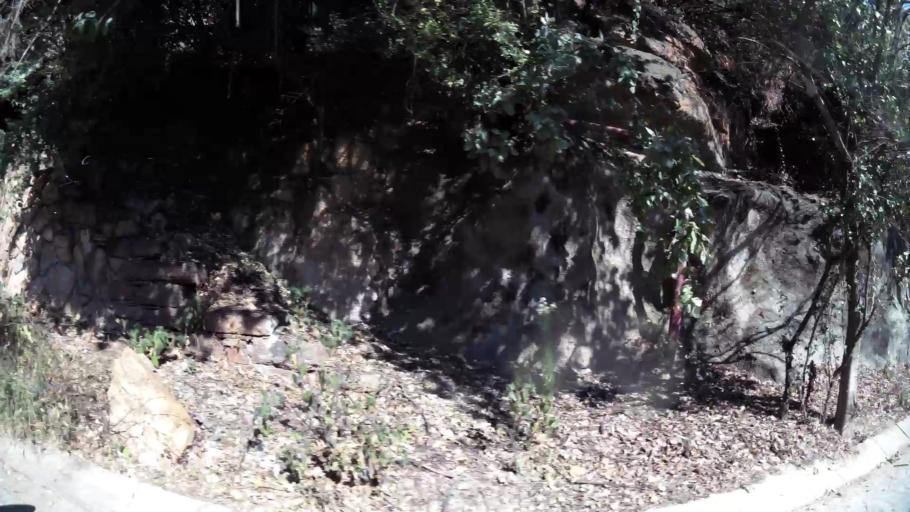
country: ZA
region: Gauteng
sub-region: City of Johannesburg Metropolitan Municipality
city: Johannesburg
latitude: -26.1675
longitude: 28.0928
